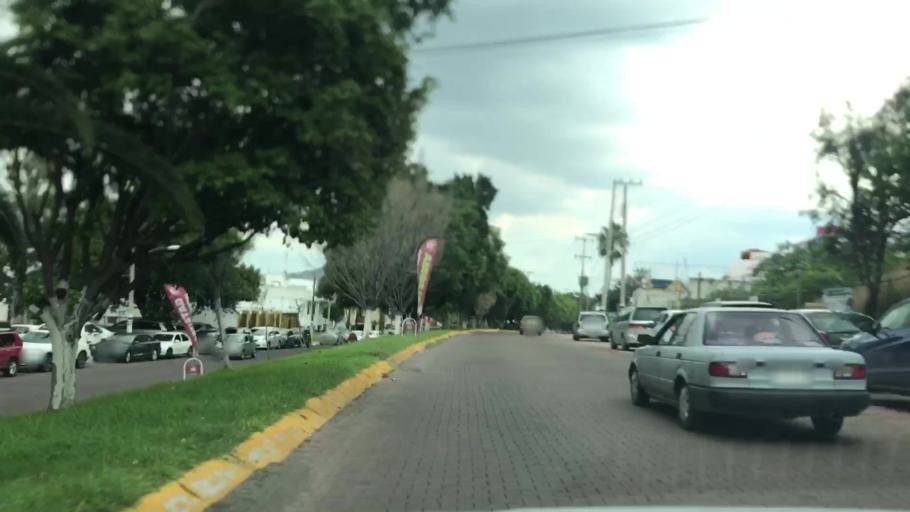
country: MX
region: Jalisco
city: Guadalajara
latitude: 20.6189
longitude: -103.4046
